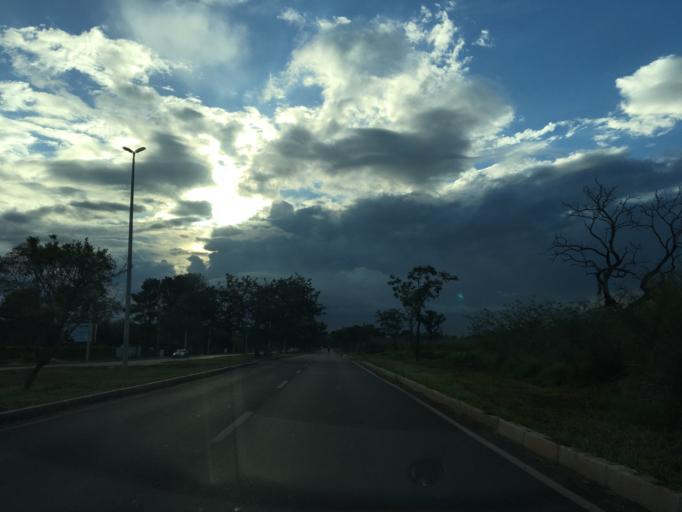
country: BR
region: Federal District
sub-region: Brasilia
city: Brasilia
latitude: -15.8144
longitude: -47.8512
